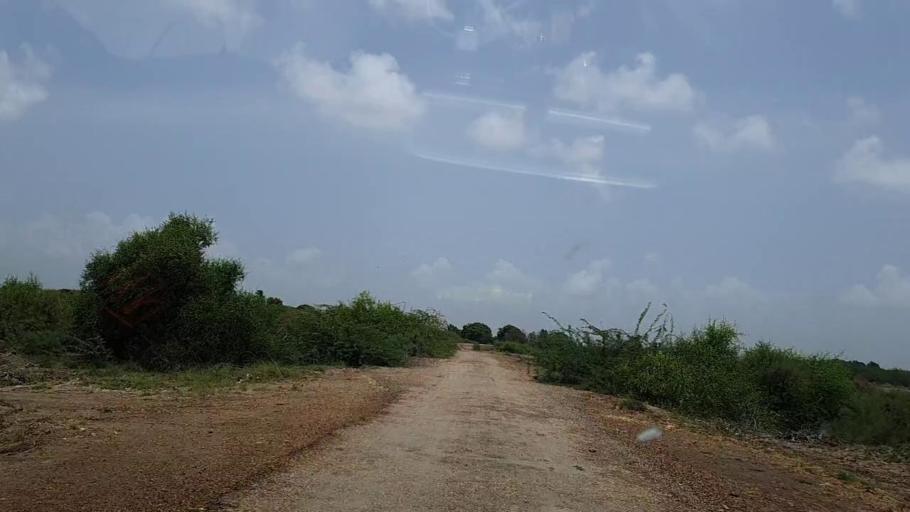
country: PK
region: Sindh
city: Keti Bandar
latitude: 24.1664
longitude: 67.5437
